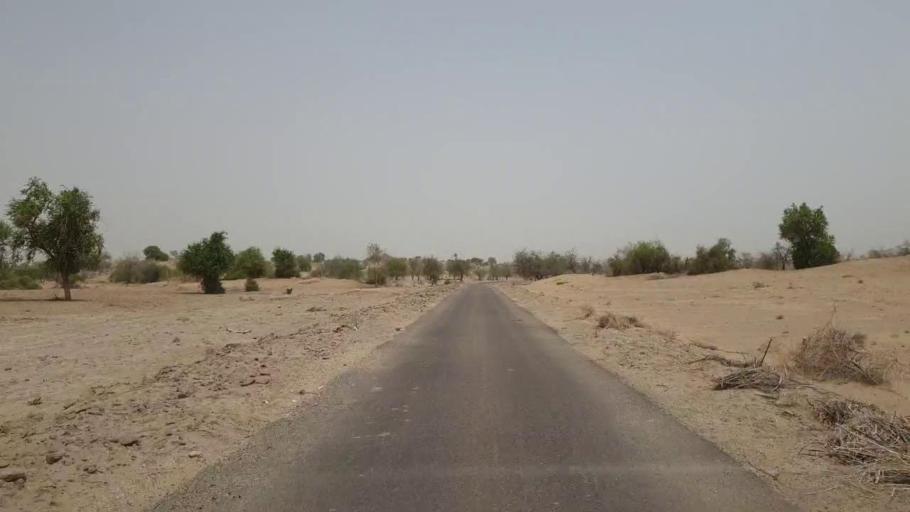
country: PK
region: Sindh
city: Islamkot
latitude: 24.8049
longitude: 70.5381
